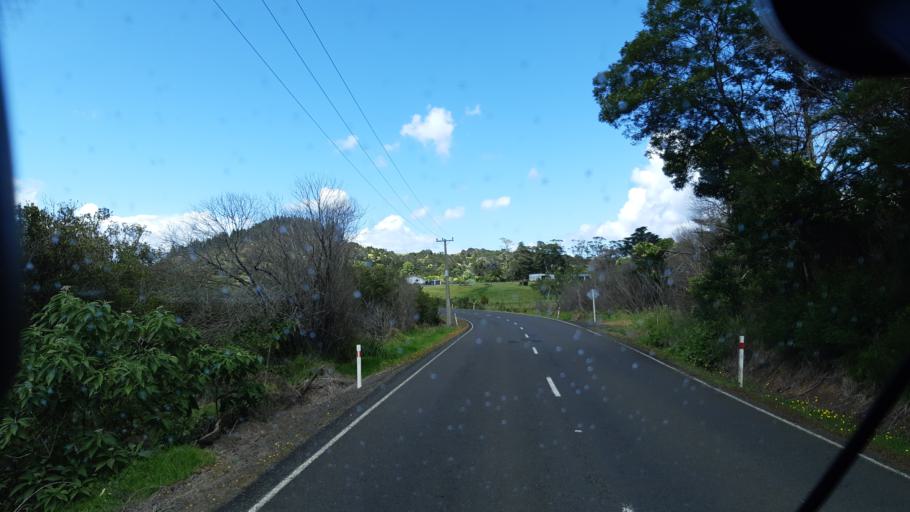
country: NZ
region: Northland
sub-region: Far North District
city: Taipa
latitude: -35.2714
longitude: 173.5226
